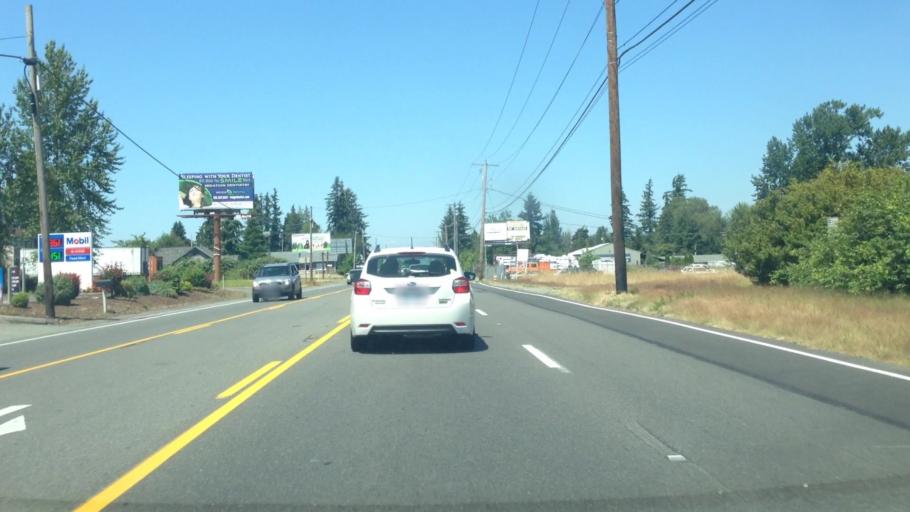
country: US
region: Washington
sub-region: Pierce County
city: North Puyallup
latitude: 47.2258
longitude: -122.2940
